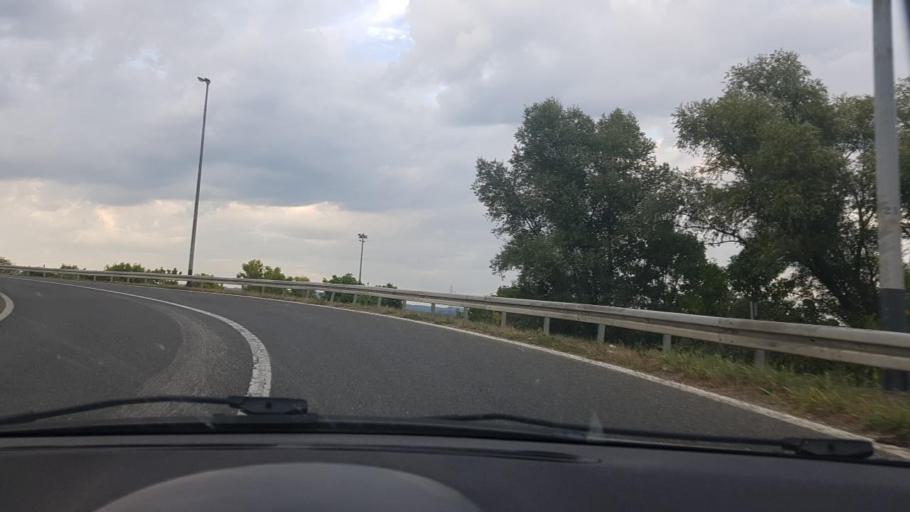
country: HR
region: Grad Zagreb
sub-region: Sesvete
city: Sesvete
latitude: 45.8498
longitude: 16.1501
